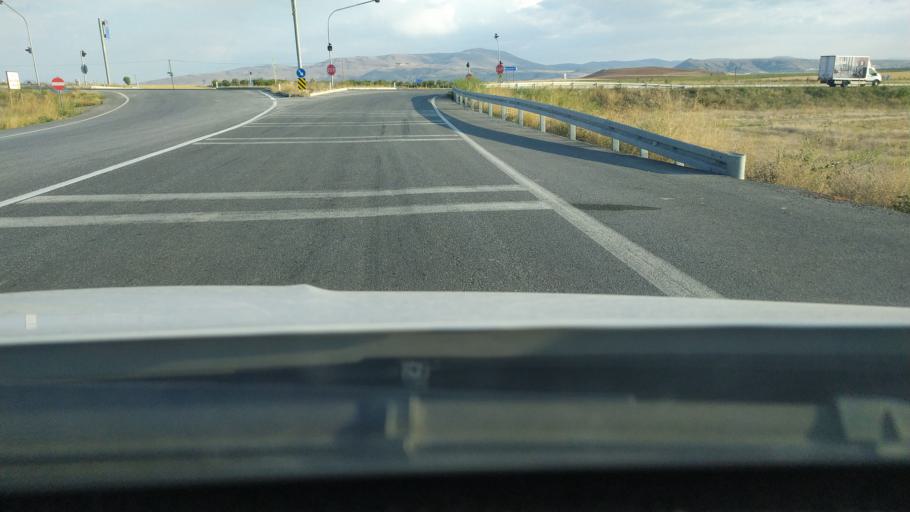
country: TR
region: Kayseri
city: Bunyan
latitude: 38.9067
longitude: 35.7574
